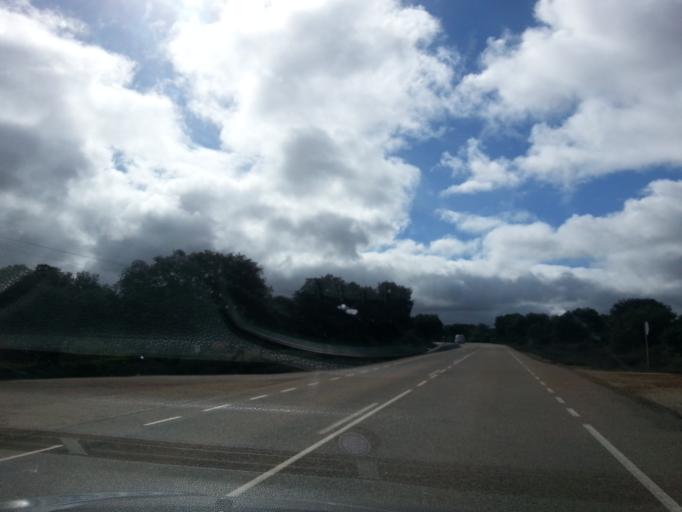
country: ES
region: Castille and Leon
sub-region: Provincia de Salamanca
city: Abusejo
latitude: 40.6860
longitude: -6.1323
